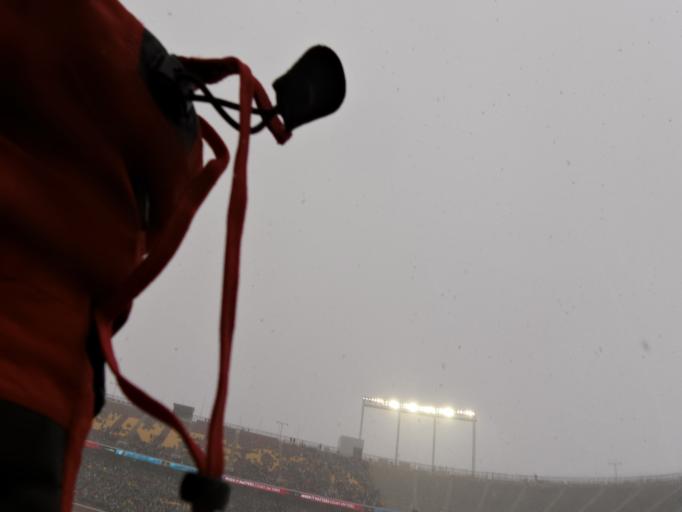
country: US
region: Minnesota
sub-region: Ramsey County
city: Lauderdale
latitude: 44.9796
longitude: -93.2250
